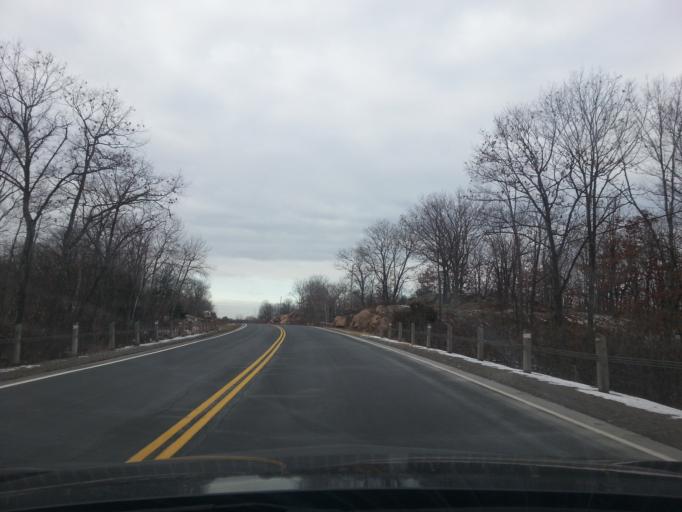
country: CA
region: Ontario
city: Greater Napanee
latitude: 44.6255
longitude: -77.1642
